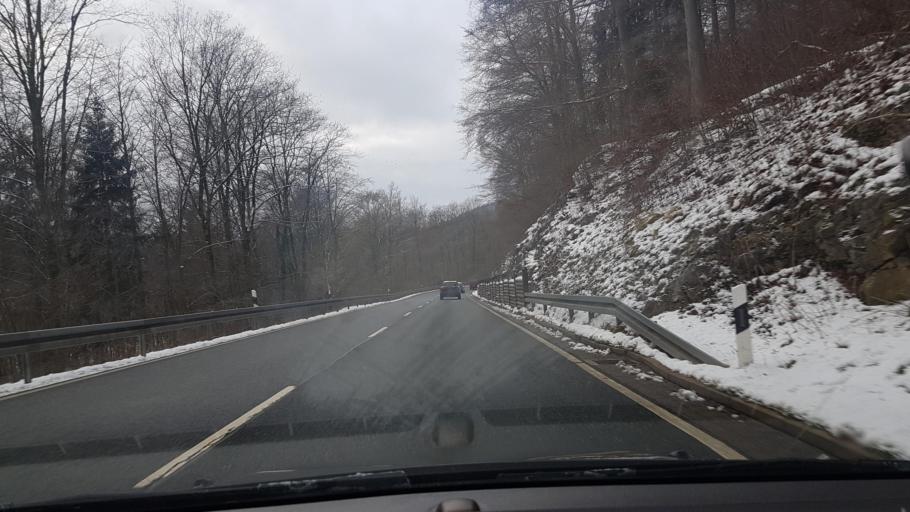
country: DE
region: Lower Saxony
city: Bad Grund
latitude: 51.8163
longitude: 10.2500
